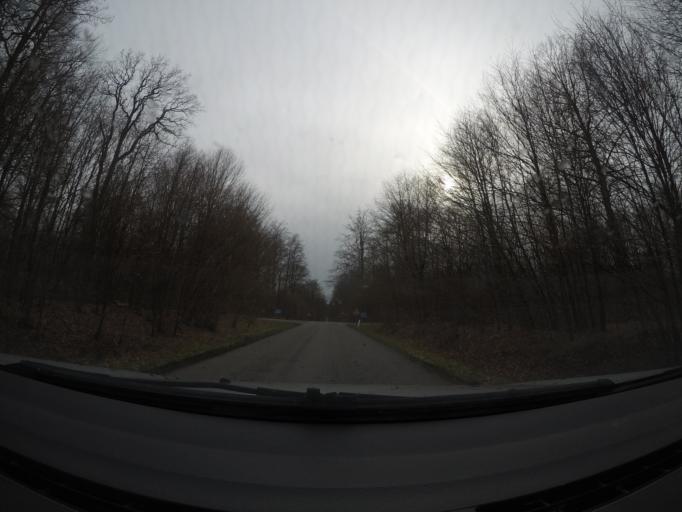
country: BE
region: Wallonia
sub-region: Province du Luxembourg
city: Martelange
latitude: 49.7827
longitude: 5.6853
